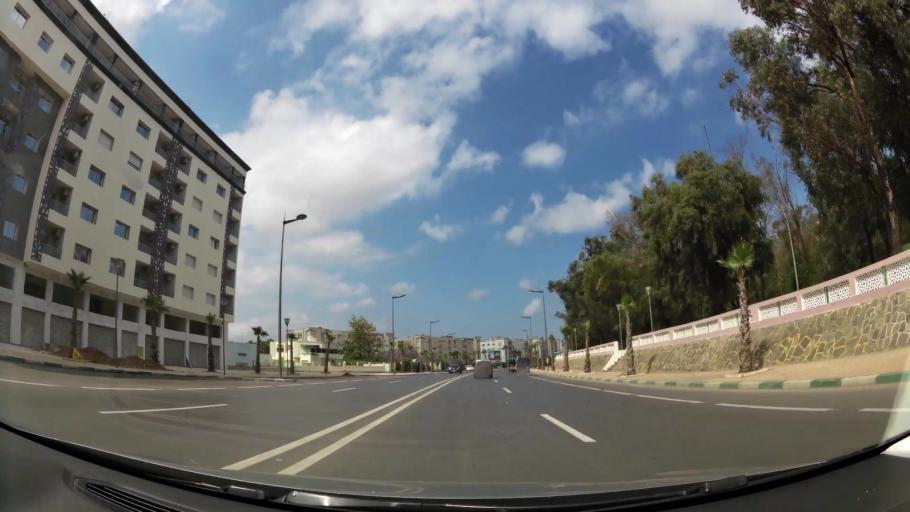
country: MA
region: Gharb-Chrarda-Beni Hssen
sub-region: Kenitra Province
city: Kenitra
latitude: 34.2504
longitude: -6.6040
